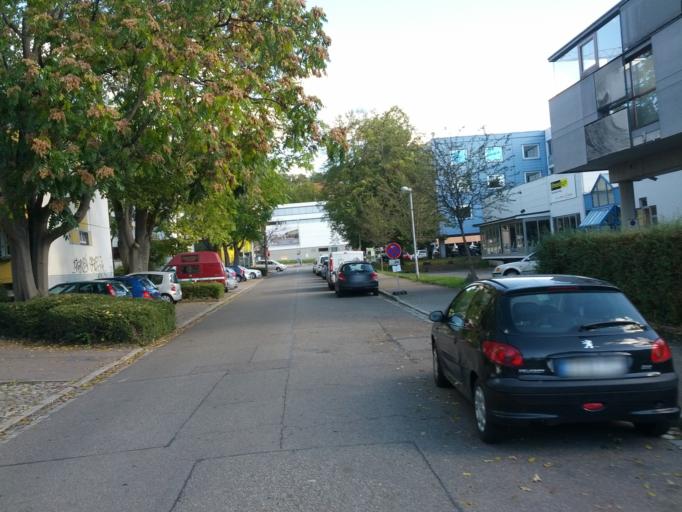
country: DE
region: Baden-Wuerttemberg
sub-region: Freiburg Region
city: Merzhausen
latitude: 47.9799
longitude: 7.8300
